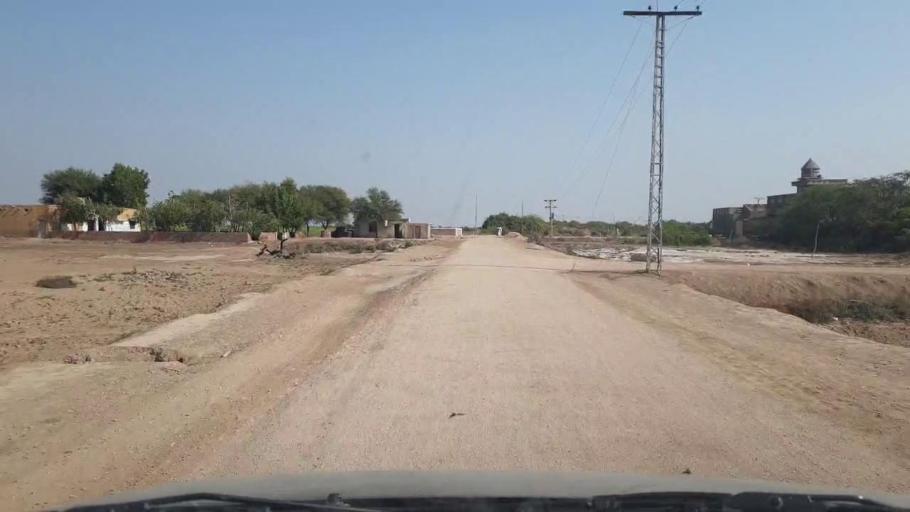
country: PK
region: Sindh
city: Samaro
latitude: 25.1794
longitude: 69.3369
